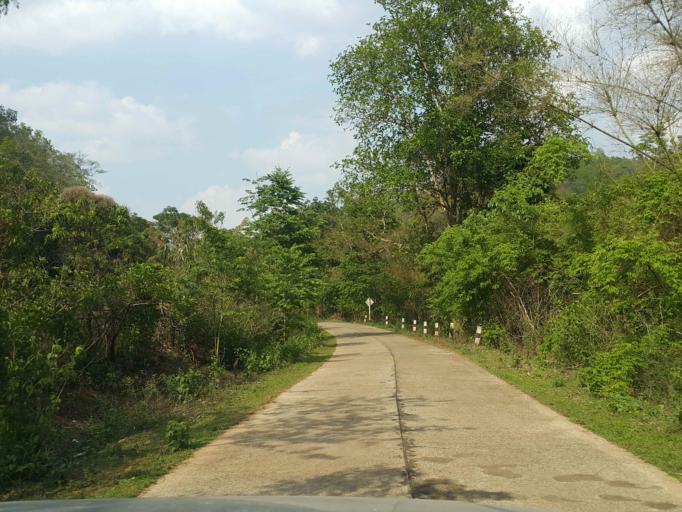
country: TH
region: Chiang Mai
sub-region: Amphoe Chiang Dao
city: Chiang Dao
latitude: 19.4019
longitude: 98.7811
